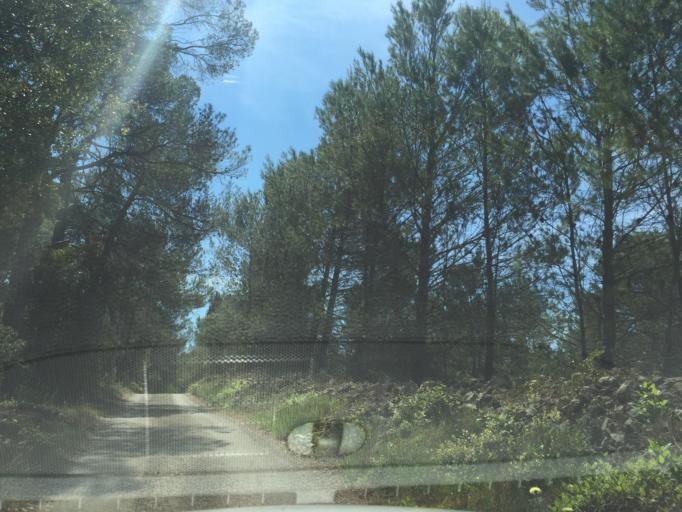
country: FR
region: Provence-Alpes-Cote d'Azur
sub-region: Departement du Var
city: Lorgues
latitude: 43.4736
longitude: 6.3701
